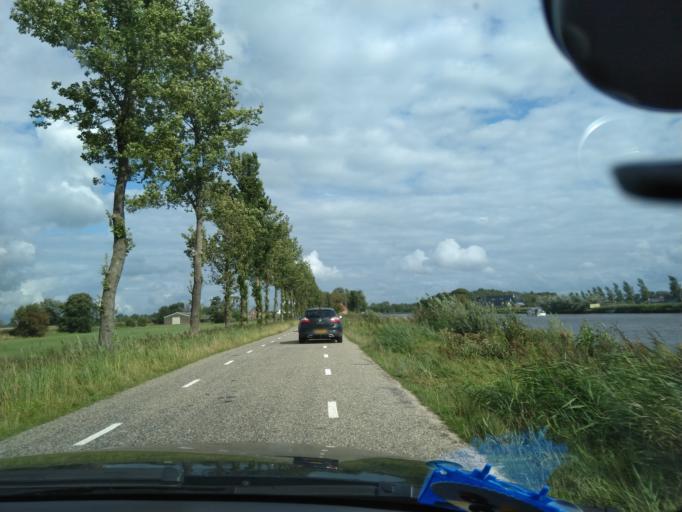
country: NL
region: Groningen
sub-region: Gemeente Zuidhorn
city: Noordhorn
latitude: 53.2550
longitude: 6.3731
